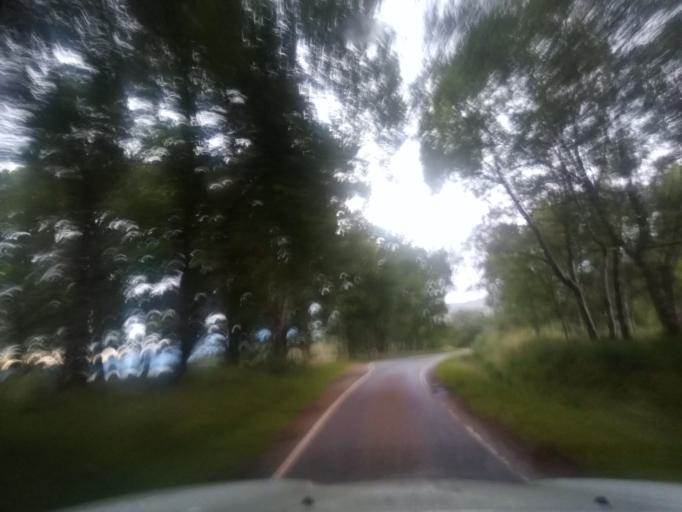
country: GB
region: Scotland
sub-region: Highland
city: Fort William
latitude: 56.8485
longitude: -5.3178
